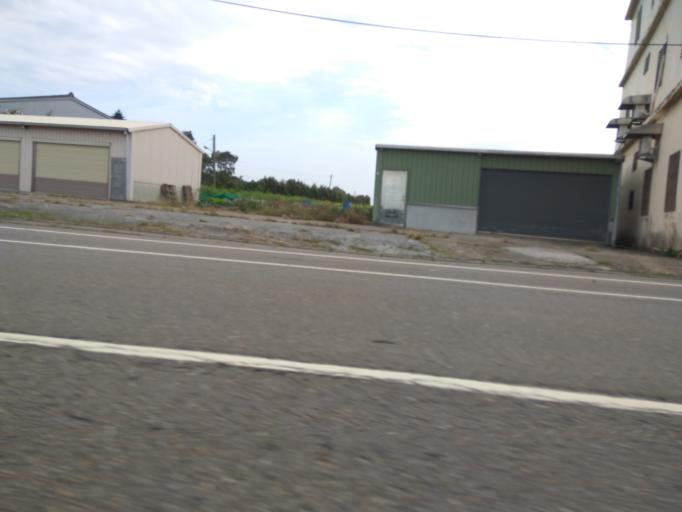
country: TW
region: Taiwan
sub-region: Hsinchu
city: Zhubei
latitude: 24.9776
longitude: 121.0269
